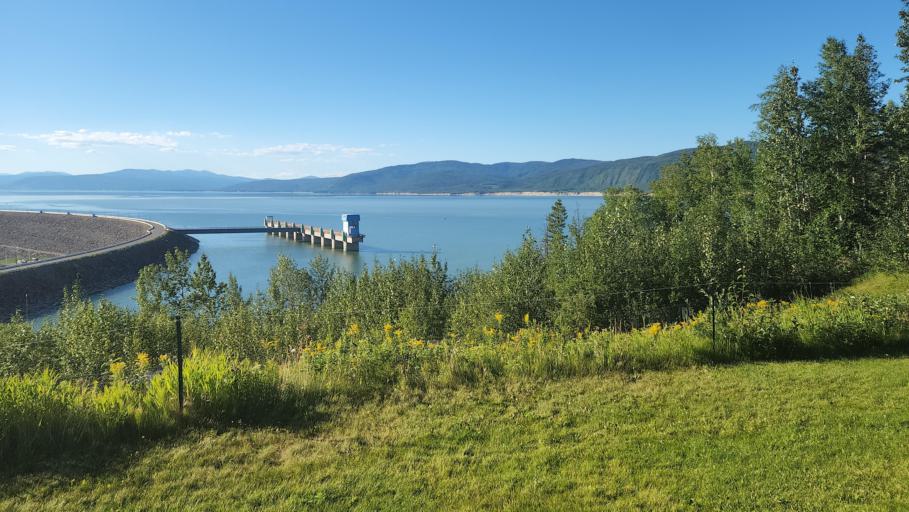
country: CA
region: British Columbia
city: Chetwynd
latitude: 56.0122
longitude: -122.1895
